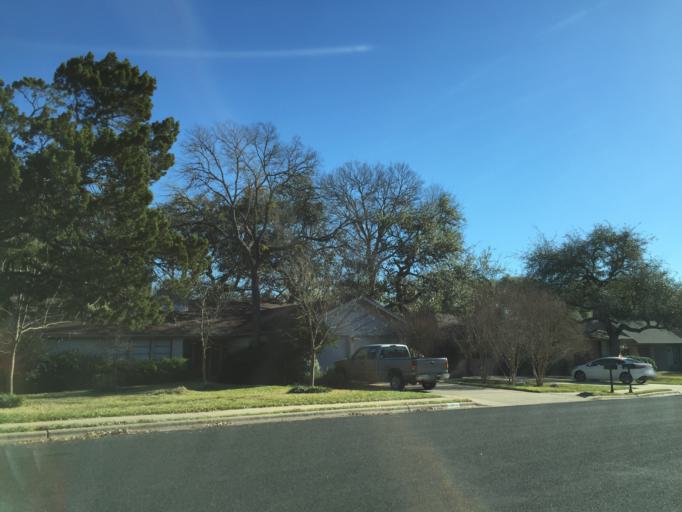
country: US
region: Texas
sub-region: Williamson County
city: Jollyville
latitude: 30.4026
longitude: -97.7349
